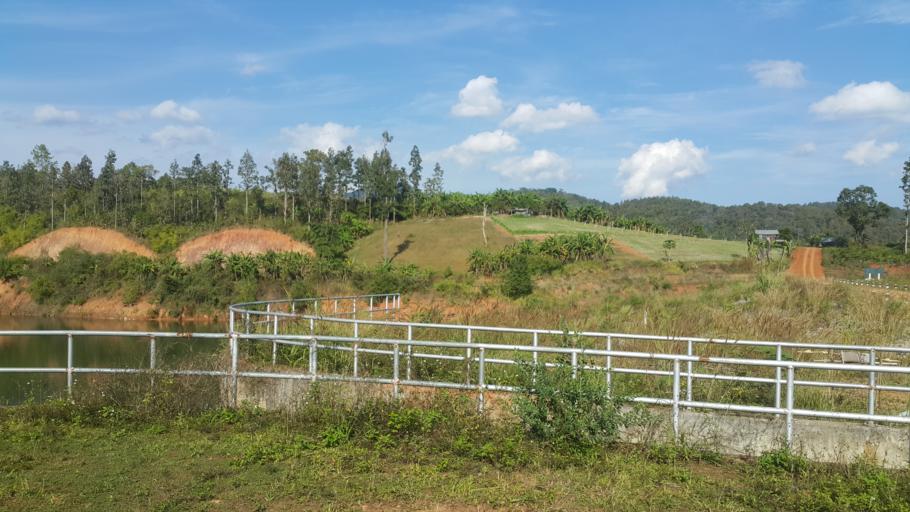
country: TH
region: Chiang Mai
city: Samoeng
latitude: 18.9529
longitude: 98.6718
